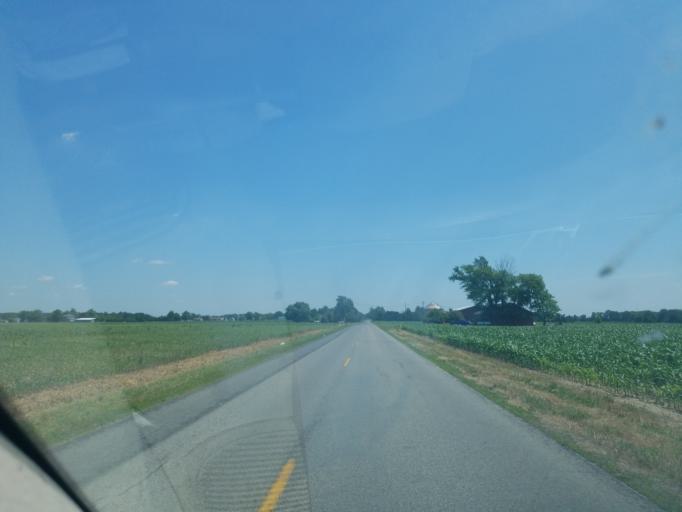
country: US
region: Ohio
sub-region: Allen County
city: Elida
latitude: 40.7873
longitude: -84.2538
